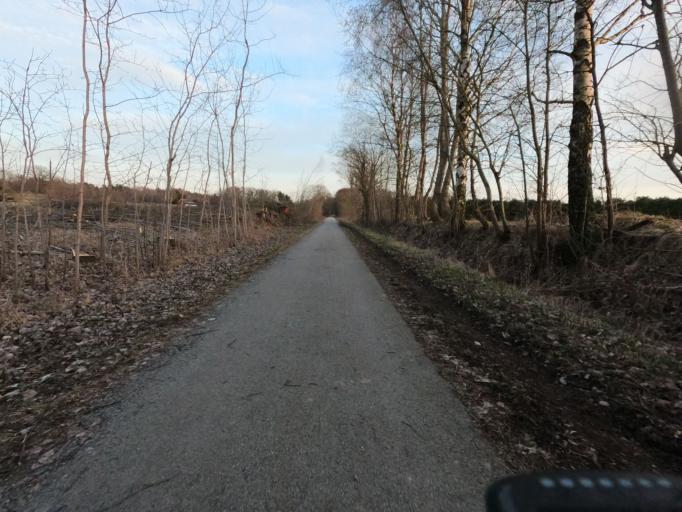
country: SE
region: Blekinge
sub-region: Karlshamns Kommun
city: Svangsta
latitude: 56.2285
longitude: 14.8136
